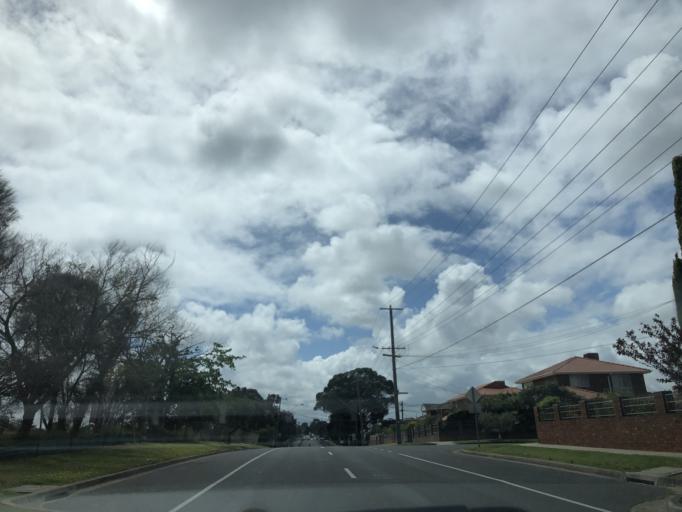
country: AU
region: Victoria
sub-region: Monash
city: Oakleigh South
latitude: -37.9340
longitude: 145.0935
